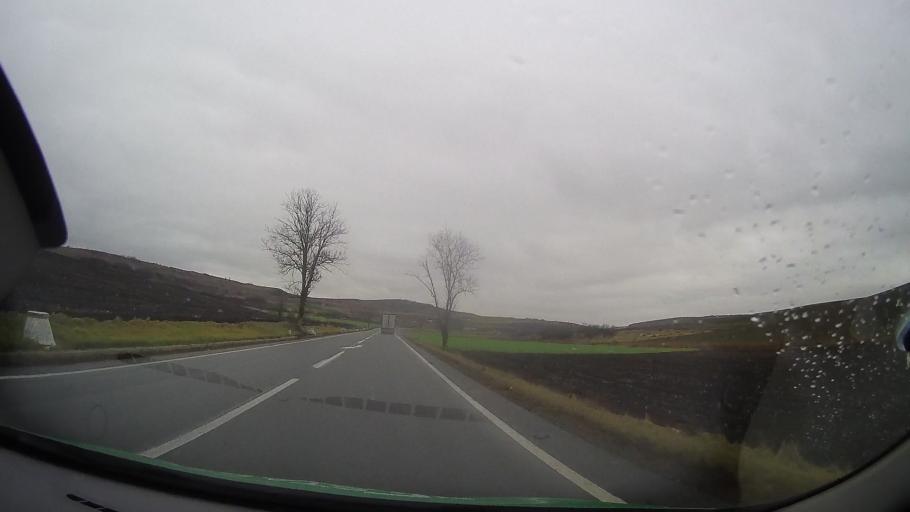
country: RO
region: Mures
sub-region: Comuna Lunca
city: Lunca
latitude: 46.8742
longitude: 24.5461
